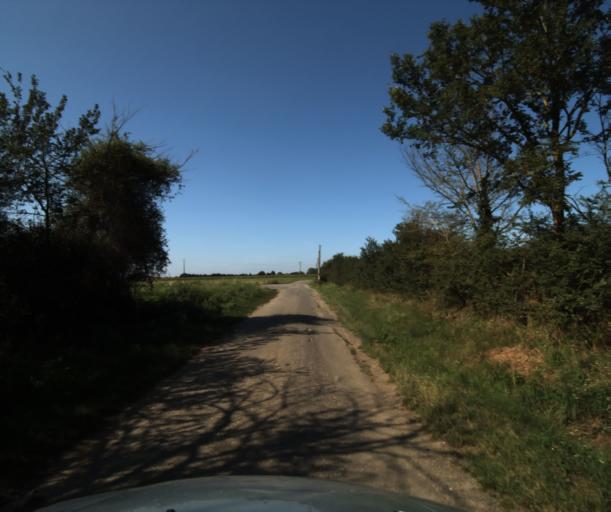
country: FR
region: Midi-Pyrenees
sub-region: Departement de la Haute-Garonne
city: Lacasse
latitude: 43.3806
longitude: 1.2561
